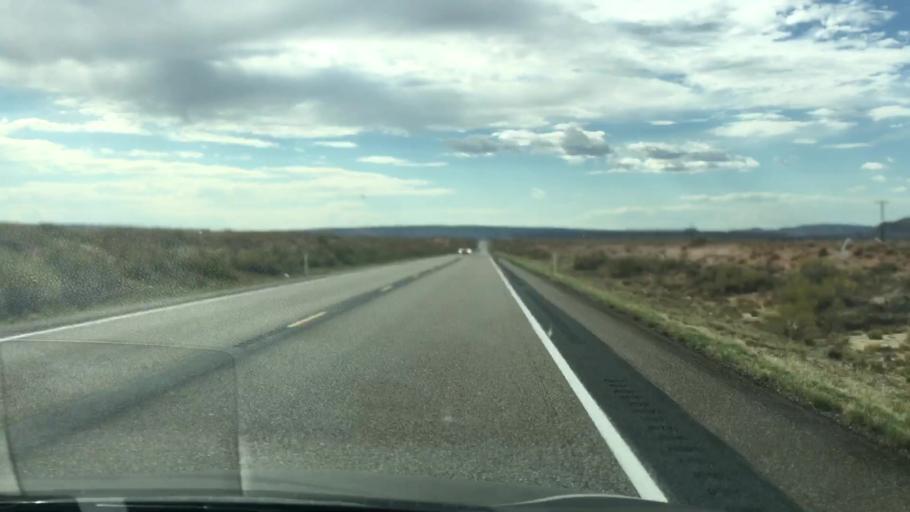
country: US
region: Arizona
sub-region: Coconino County
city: Page
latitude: 37.0990
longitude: -111.7869
